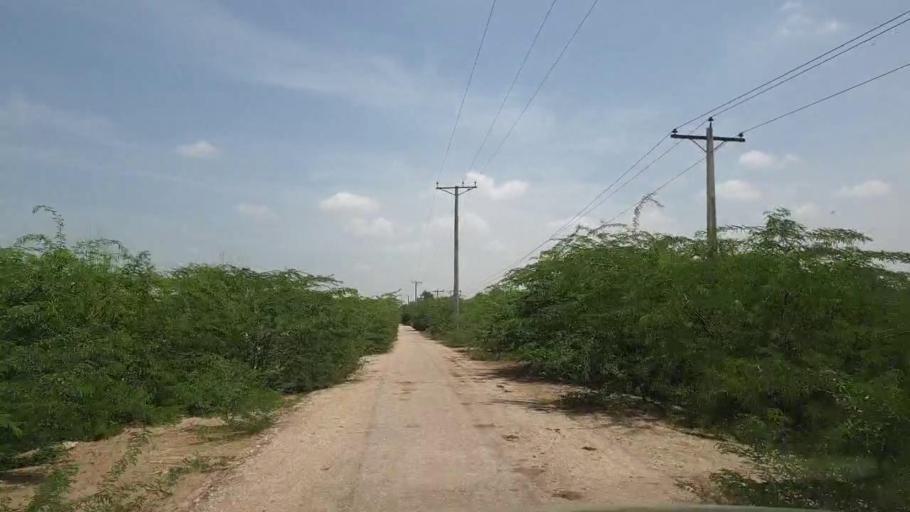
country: PK
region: Sindh
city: Kot Diji
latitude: 27.1276
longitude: 69.0000
